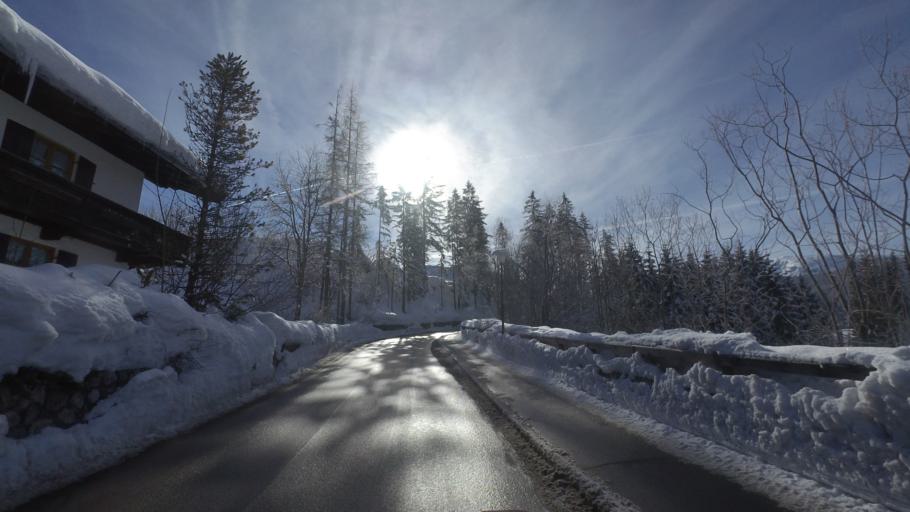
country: DE
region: Bavaria
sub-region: Upper Bavaria
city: Reit im Winkl
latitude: 47.6691
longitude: 12.4763
